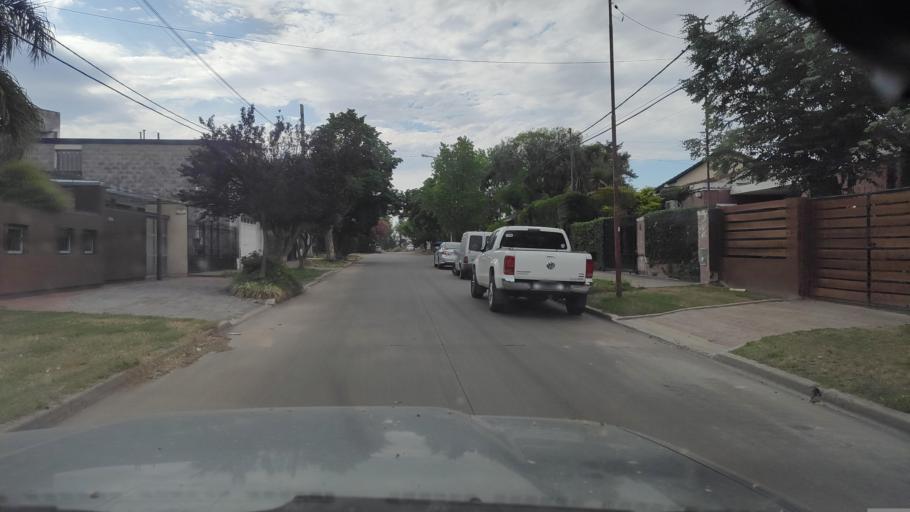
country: AR
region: Buenos Aires
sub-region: Partido de Lujan
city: Lujan
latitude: -34.5602
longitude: -59.1039
